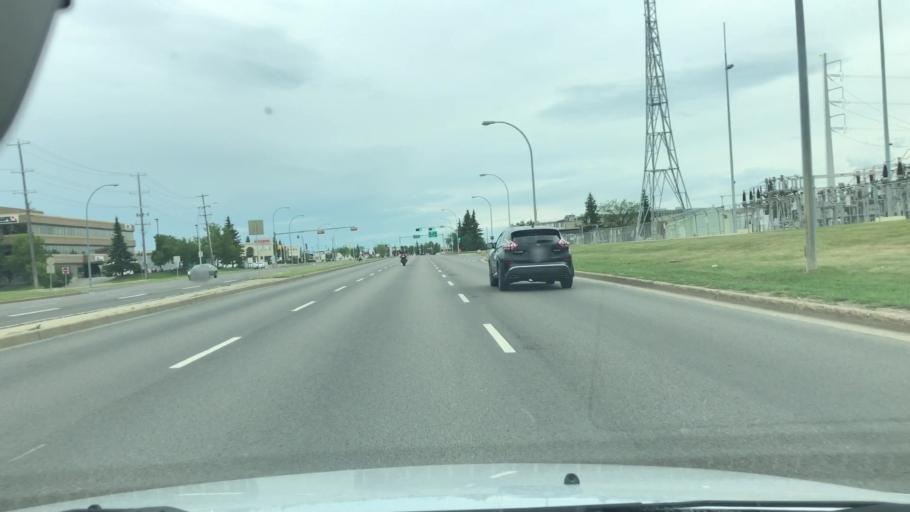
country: CA
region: Alberta
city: St. Albert
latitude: 53.5501
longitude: -113.6155
